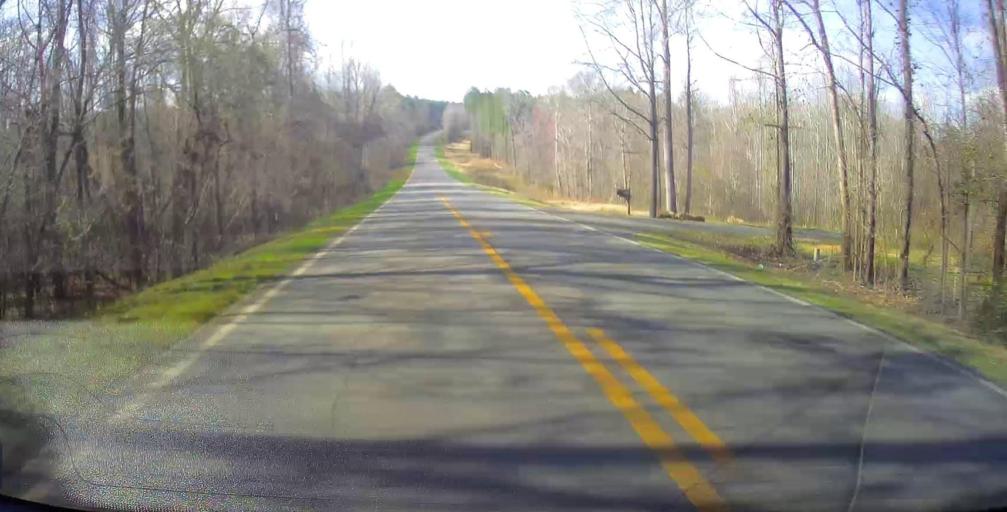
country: US
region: Georgia
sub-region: Laurens County
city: Dublin
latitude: 32.5726
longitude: -83.0438
